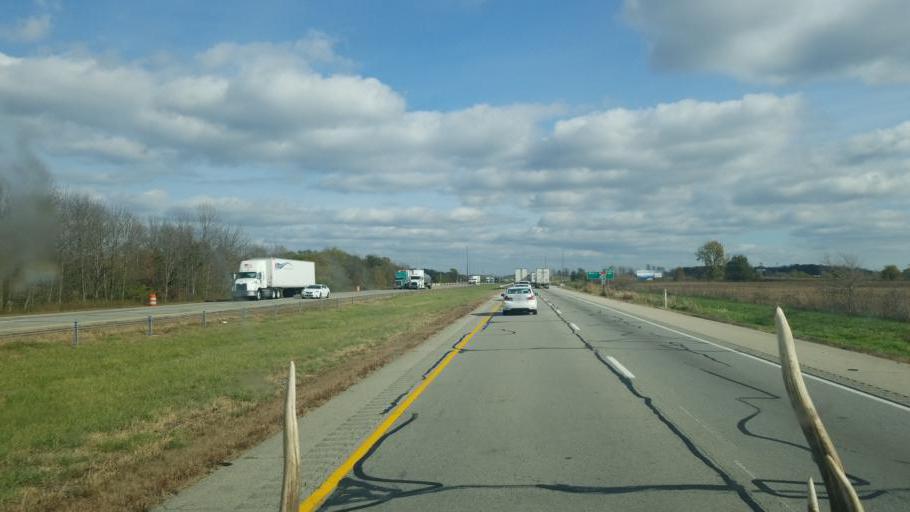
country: US
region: Indiana
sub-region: Wayne County
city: Cambridge City
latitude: 39.8520
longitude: -85.2736
